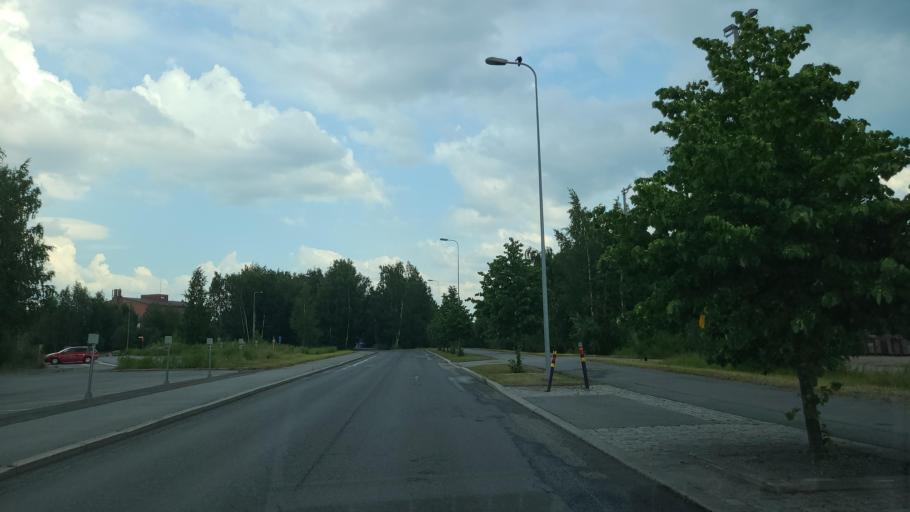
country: FI
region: Ostrobothnia
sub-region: Vaasa
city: Vaasa
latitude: 63.0957
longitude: 21.6321
